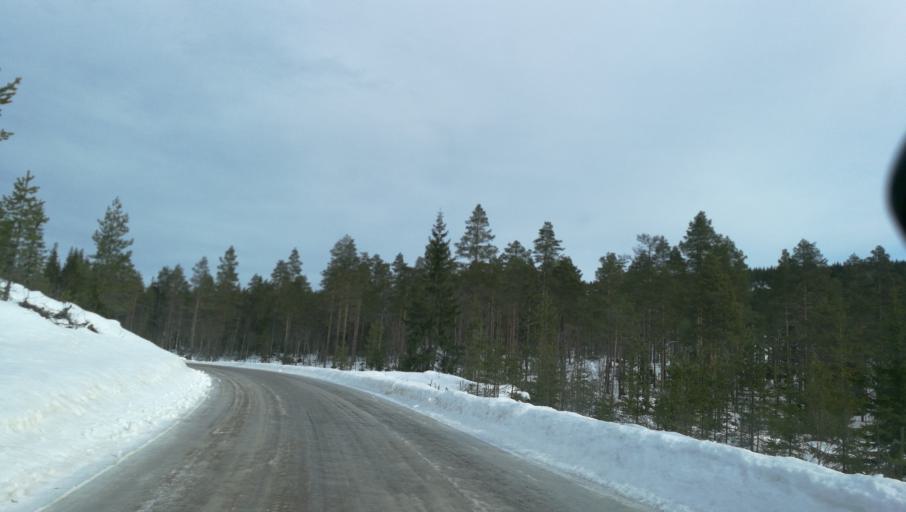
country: SE
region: Vaermland
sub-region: Torsby Kommun
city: Torsby
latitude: 60.6432
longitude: 12.7982
